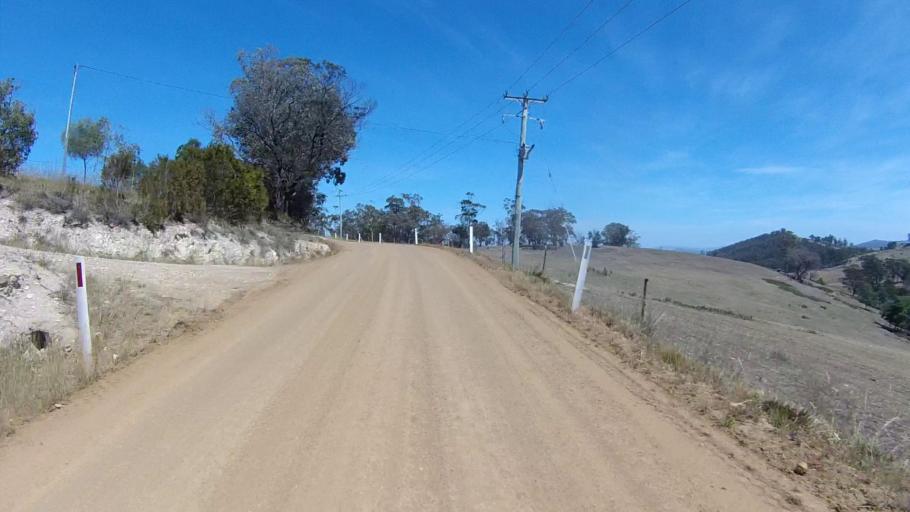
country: AU
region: Tasmania
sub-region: Sorell
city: Sorell
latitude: -42.7810
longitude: 147.6457
